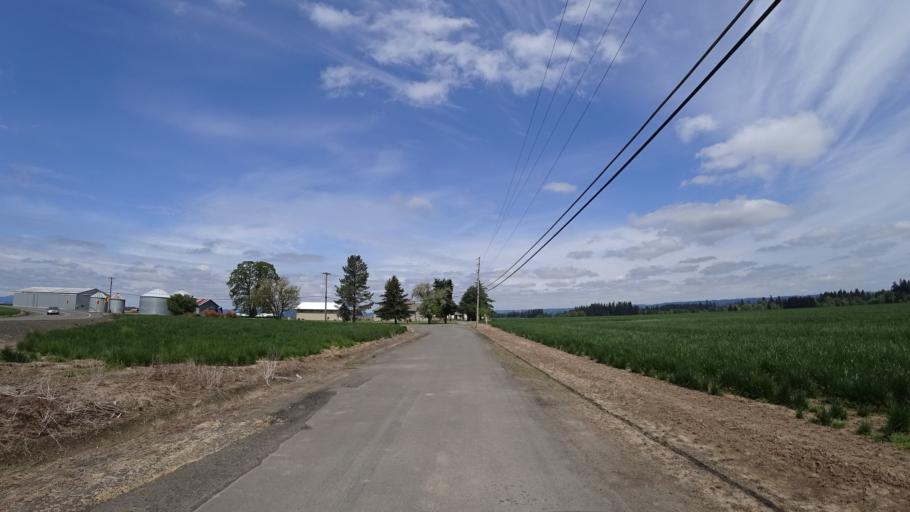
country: US
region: Oregon
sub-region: Washington County
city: North Plains
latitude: 45.5617
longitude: -122.9994
